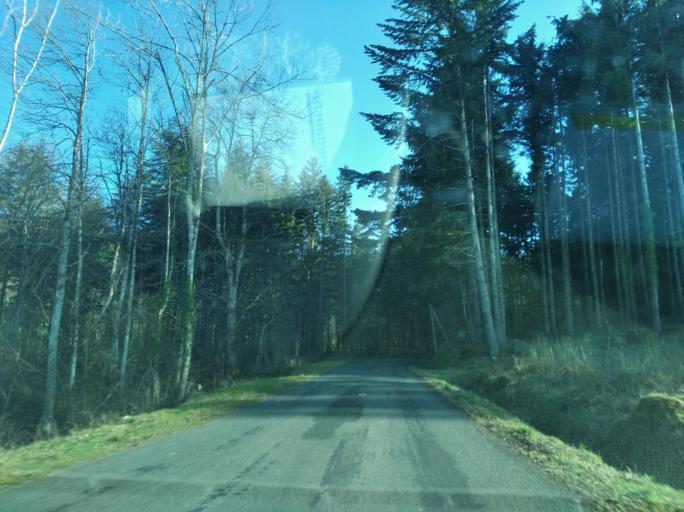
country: FR
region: Auvergne
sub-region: Departement de l'Allier
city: Le Mayet-de-Montagne
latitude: 46.0986
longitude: 3.7341
